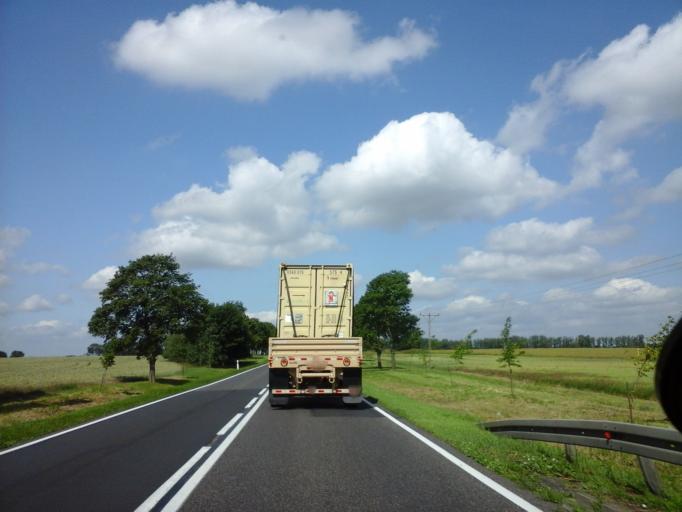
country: PL
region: West Pomeranian Voivodeship
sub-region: Powiat stargardzki
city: Stargard Szczecinski
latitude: 53.3066
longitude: 15.1428
